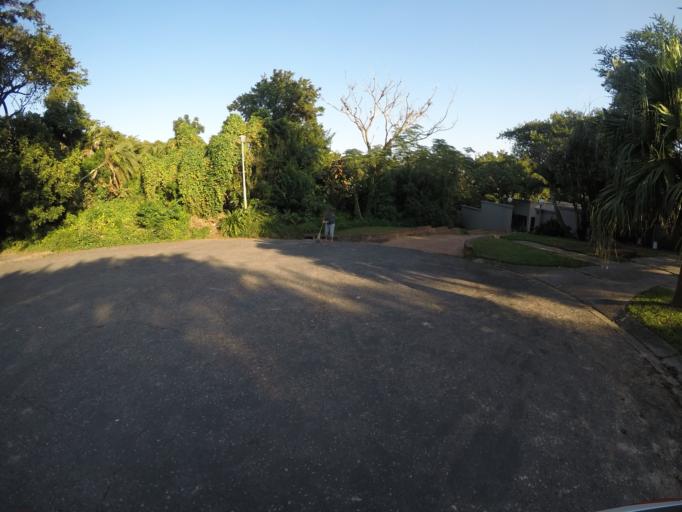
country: ZA
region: KwaZulu-Natal
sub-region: uThungulu District Municipality
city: Richards Bay
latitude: -28.7827
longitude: 32.0949
